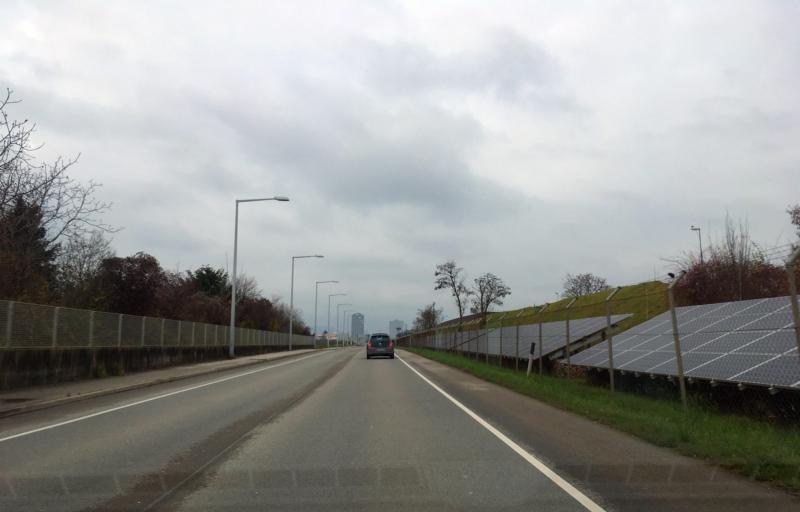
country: AT
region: Lower Austria
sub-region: Politischer Bezirk Wien-Umgebung
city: Gerasdorf bei Wien
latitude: 48.2573
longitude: 16.4846
